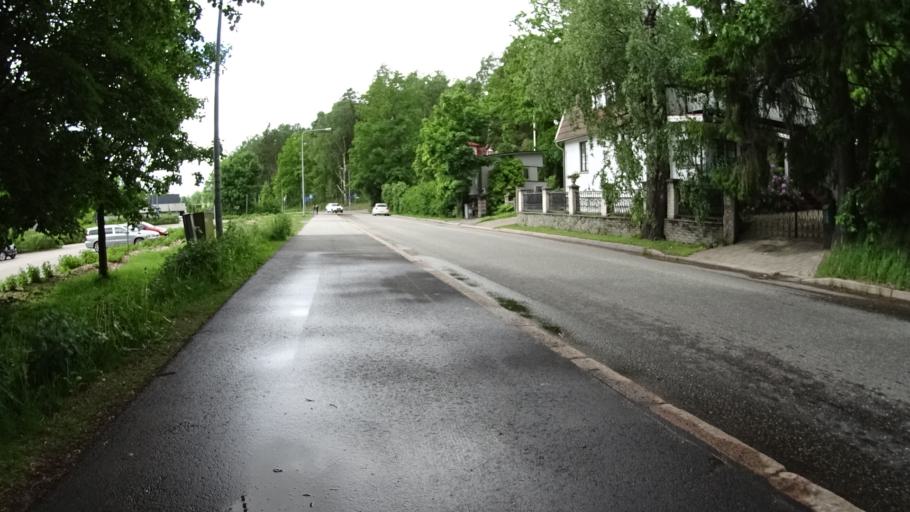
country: FI
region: Uusimaa
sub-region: Helsinki
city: Kilo
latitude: 60.2264
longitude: 24.8077
